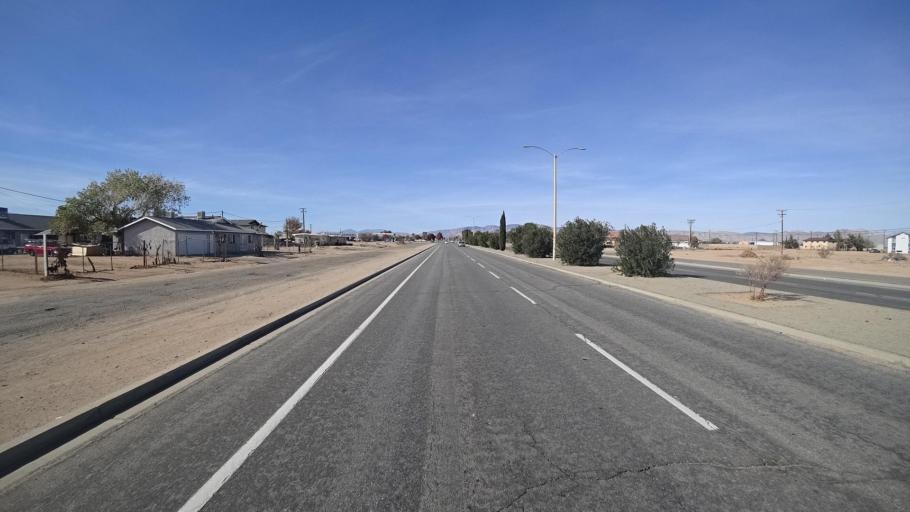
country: US
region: California
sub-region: Kern County
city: California City
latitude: 35.1258
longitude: -117.9795
